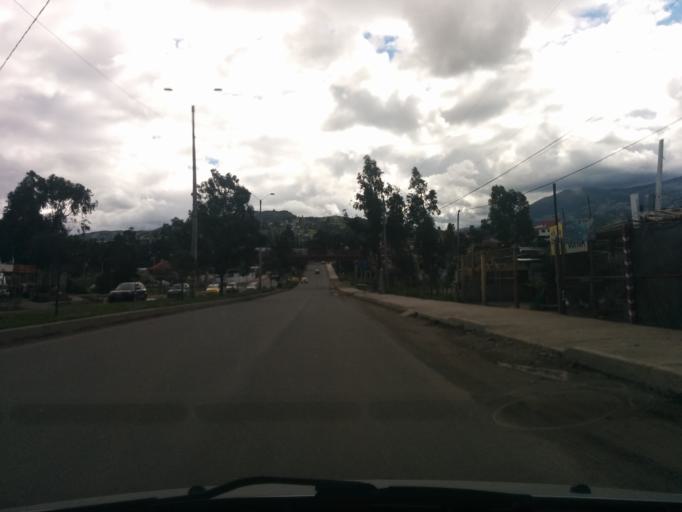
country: EC
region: Azuay
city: Cuenca
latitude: -2.9243
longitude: -79.0365
